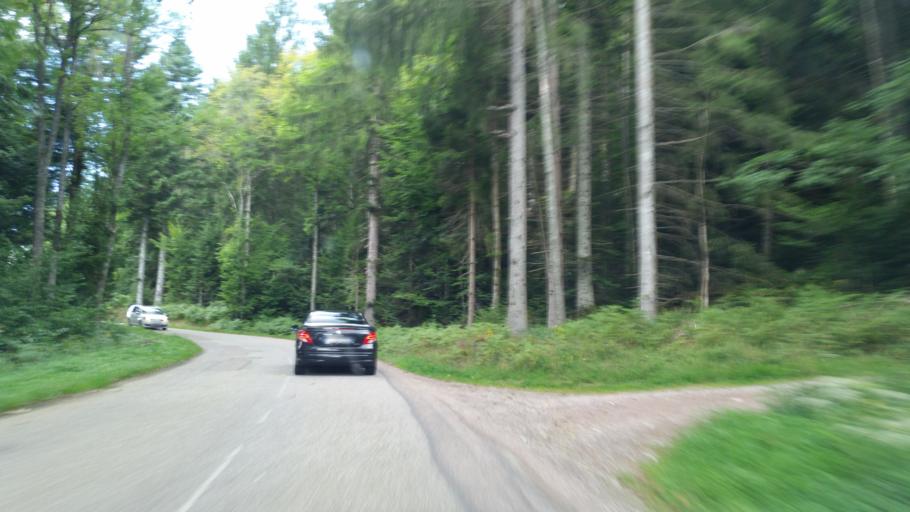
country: FR
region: Lorraine
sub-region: Departement des Vosges
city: Le Tholy
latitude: 48.0784
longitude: 6.7960
